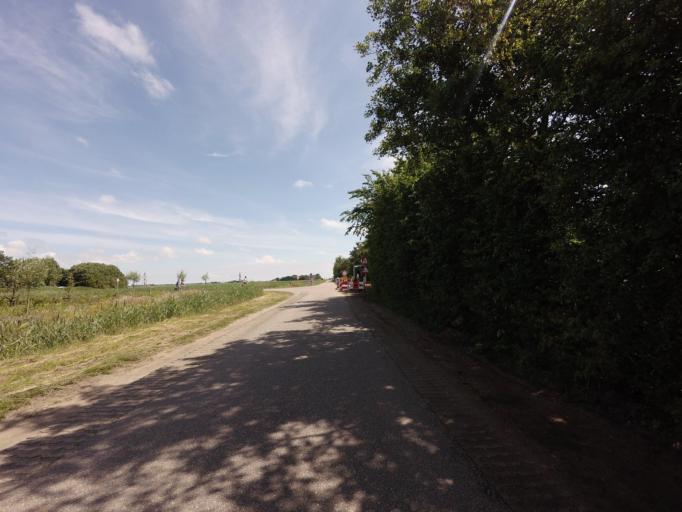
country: NL
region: North Holland
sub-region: Gemeente Texel
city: Den Burg
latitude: 53.0572
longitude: 4.8136
